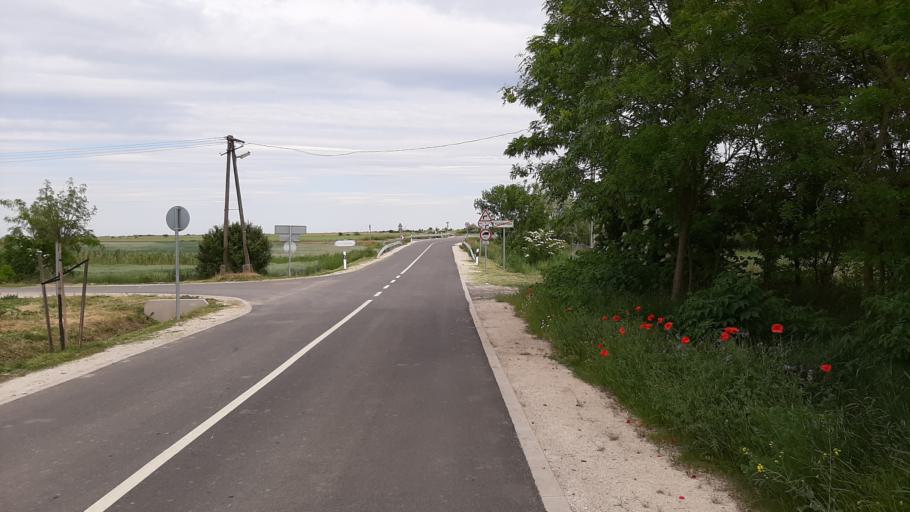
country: RO
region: Timis
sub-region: Comuna Beba Veche
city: Beba Veche
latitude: 46.1436
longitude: 20.2786
